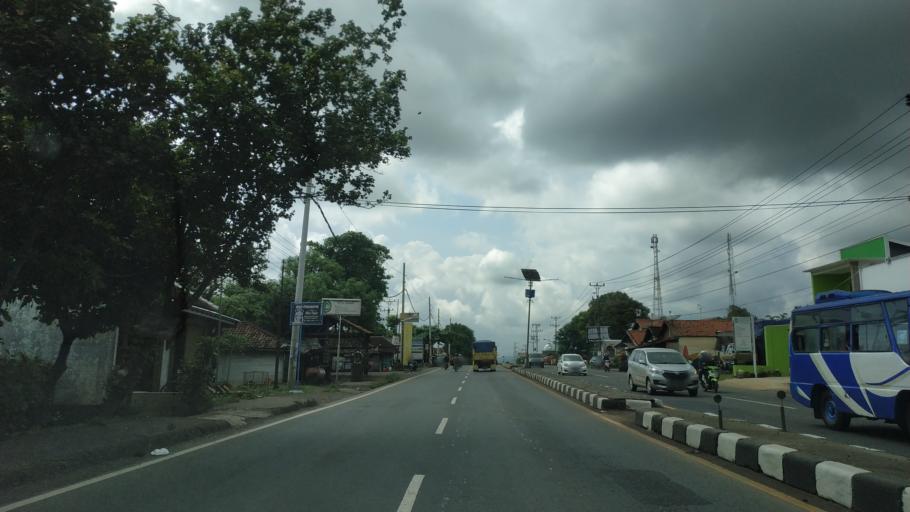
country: ID
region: Central Java
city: Pekalongan
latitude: -6.9479
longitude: 109.7848
